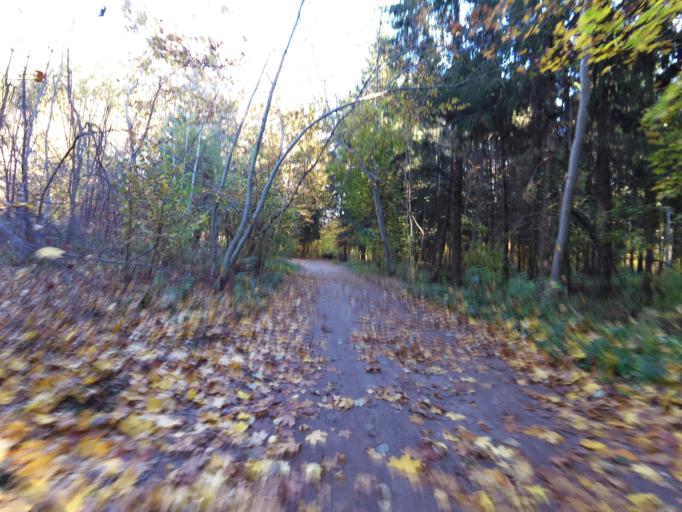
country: LT
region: Vilnius County
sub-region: Vilnius
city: Fabijoniskes
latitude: 54.7415
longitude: 25.2567
